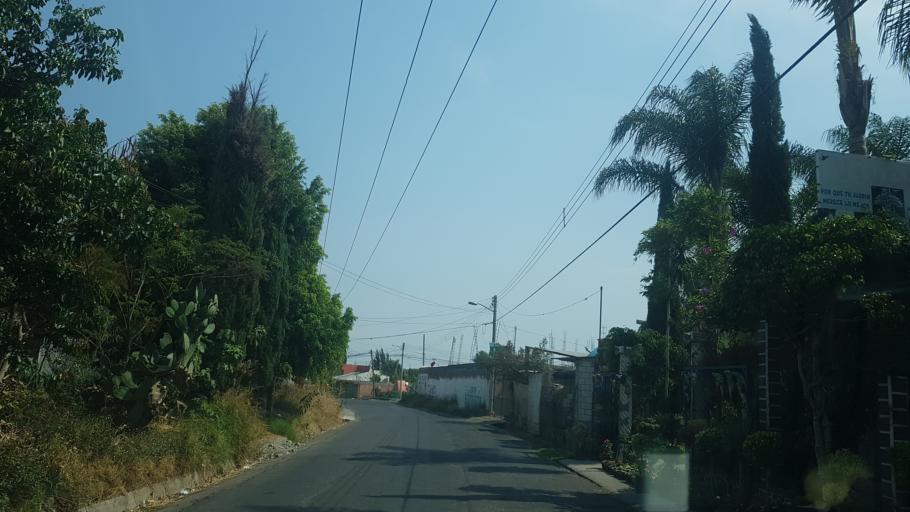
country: MX
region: Puebla
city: Atlixco
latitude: 18.9270
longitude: -98.4543
